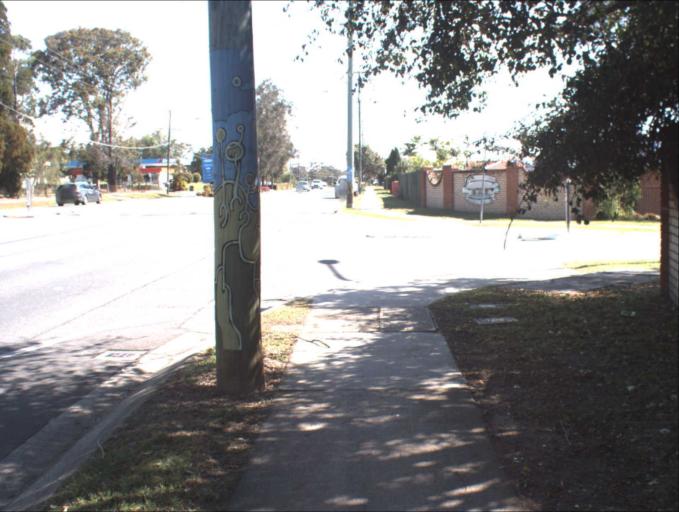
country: AU
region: Queensland
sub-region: Logan
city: Park Ridge South
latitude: -27.6756
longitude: 153.0260
